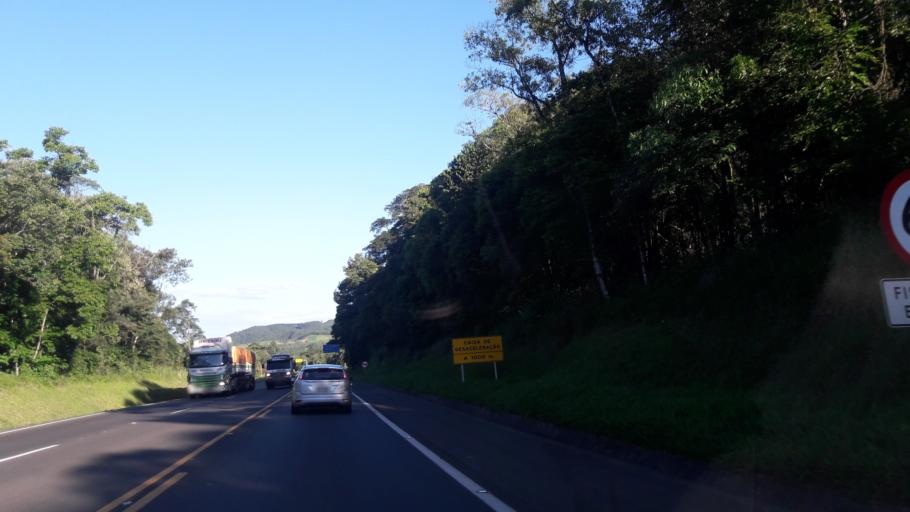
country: BR
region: Parana
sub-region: Prudentopolis
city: Prudentopolis
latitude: -25.3127
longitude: -51.1799
